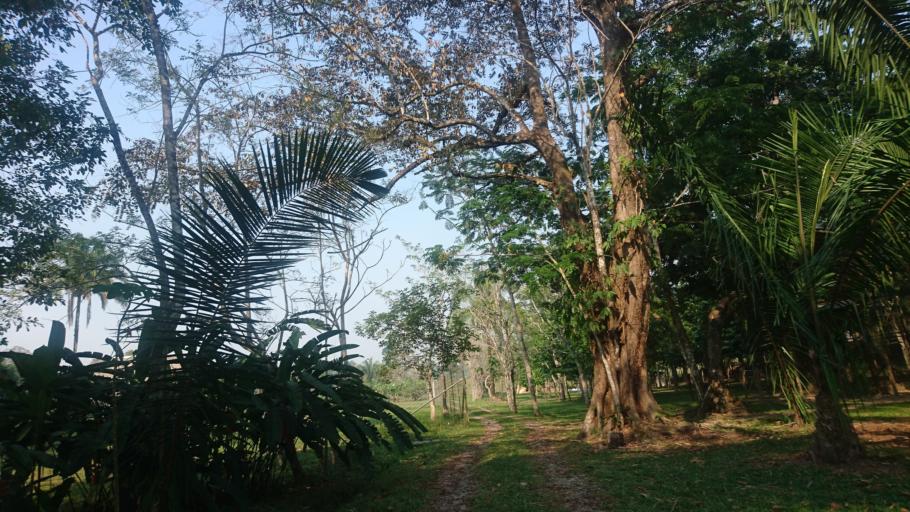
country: MX
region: Chiapas
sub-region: Marques de Comillas
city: Zamora Pico de Oro
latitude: 16.2579
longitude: -90.8622
